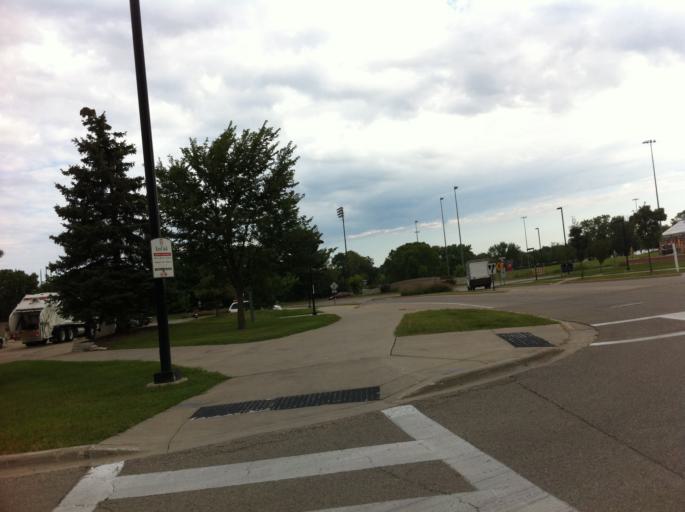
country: US
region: Wisconsin
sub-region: Dane County
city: Shorewood Hills
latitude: 43.0755
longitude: -89.4253
